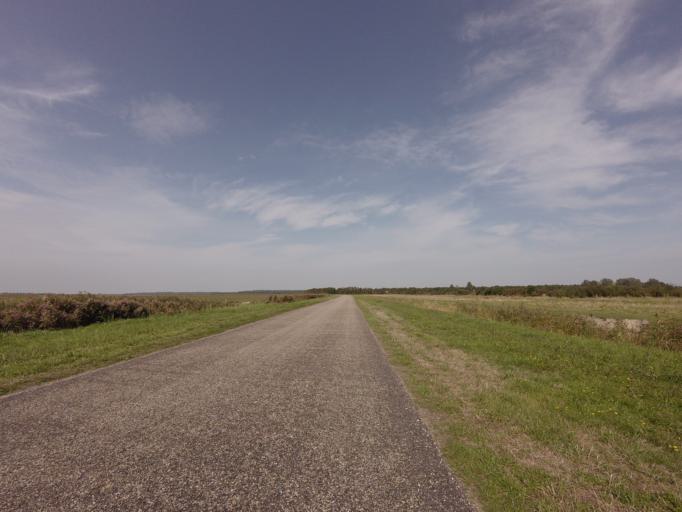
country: NL
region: Groningen
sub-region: Gemeente De Marne
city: Ulrum
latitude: 53.3532
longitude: 6.2653
